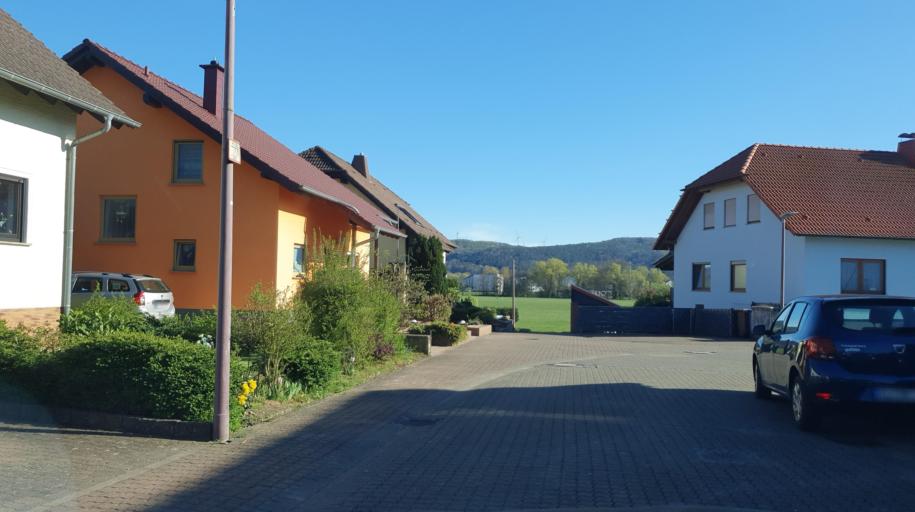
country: DE
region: Rheinland-Pfalz
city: Bruchmuhlbach-Miesau
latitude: 49.3993
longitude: 7.4407
